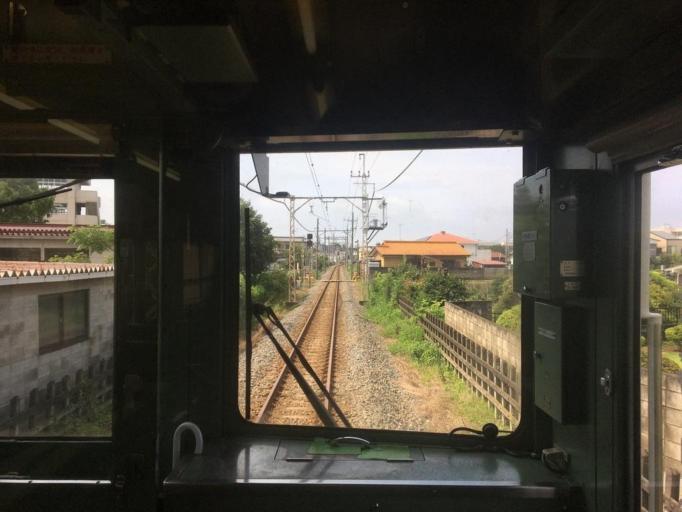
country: JP
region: Tochigi
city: Sano
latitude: 36.3250
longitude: 139.5794
